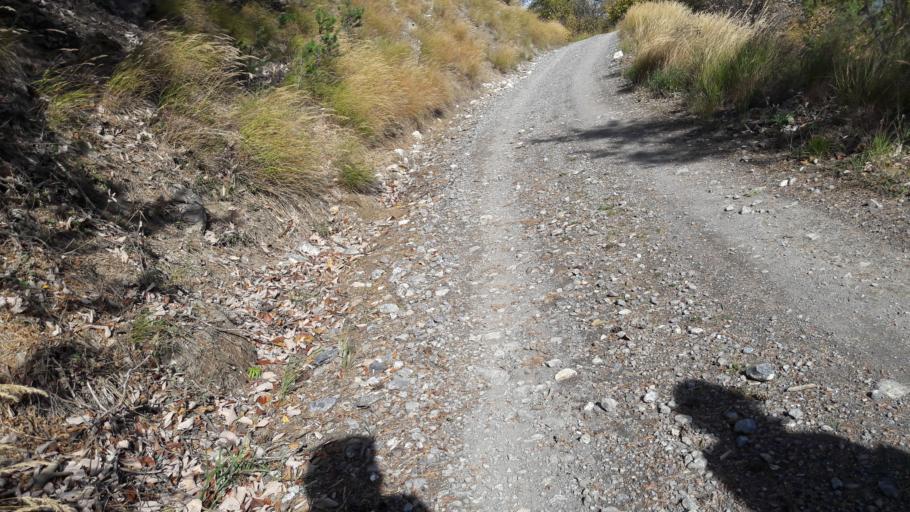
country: FR
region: Rhone-Alpes
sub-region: Departement de la Savoie
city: Valloire
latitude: 45.1915
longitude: 6.4289
